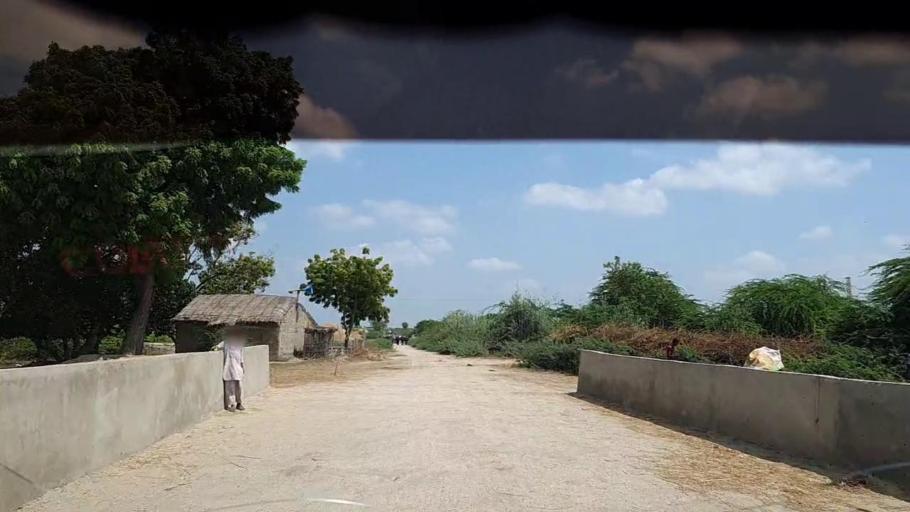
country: PK
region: Sindh
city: Kadhan
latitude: 24.5819
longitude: 68.9617
